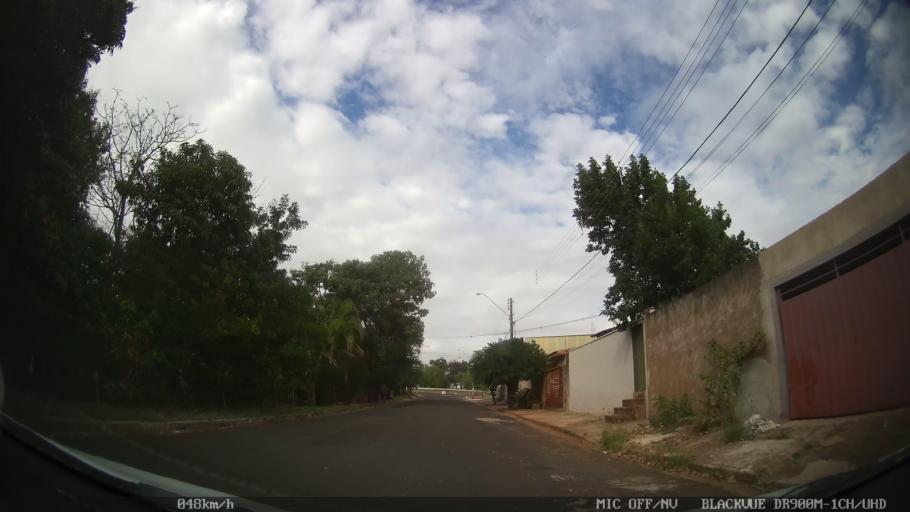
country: BR
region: Sao Paulo
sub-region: Sao Jose Do Rio Preto
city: Sao Jose do Rio Preto
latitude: -20.8244
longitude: -49.3484
